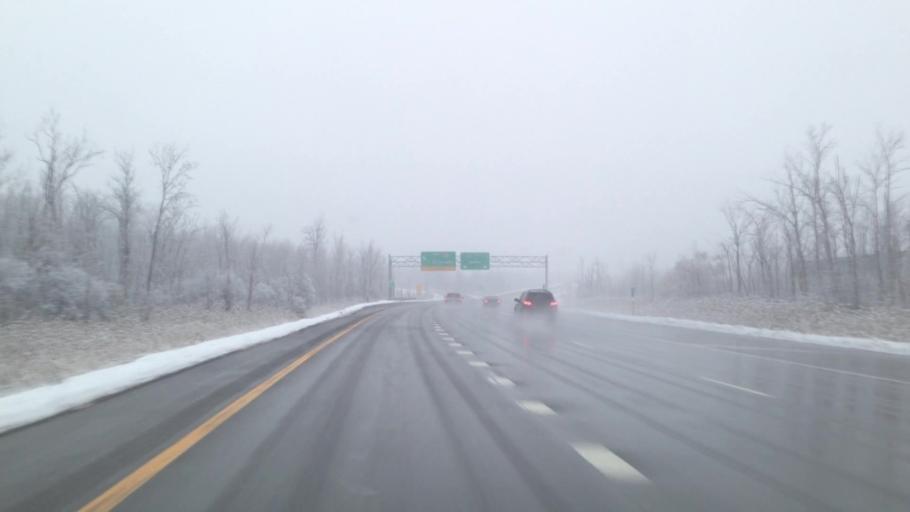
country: US
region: New York
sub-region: Onondaga County
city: East Syracuse
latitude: 43.0560
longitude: -76.0608
